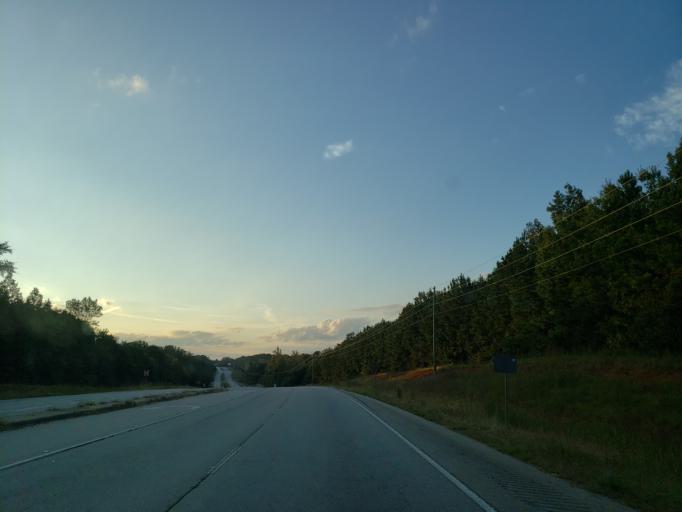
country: US
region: Georgia
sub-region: Carroll County
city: Carrollton
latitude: 33.6117
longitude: -85.0642
